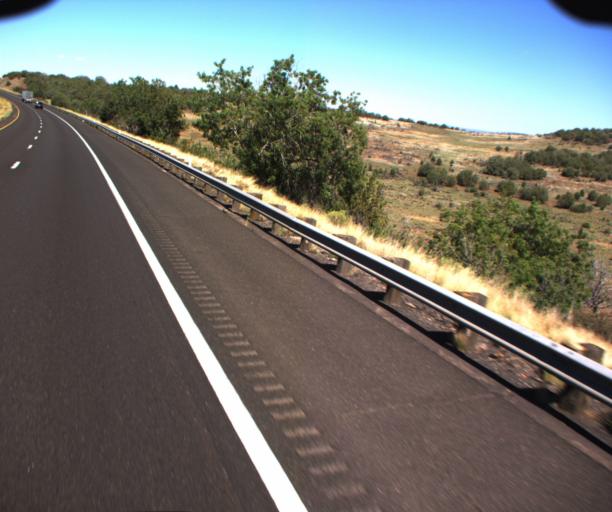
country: US
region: Arizona
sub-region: Yavapai County
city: Paulden
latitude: 35.2720
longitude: -112.7350
